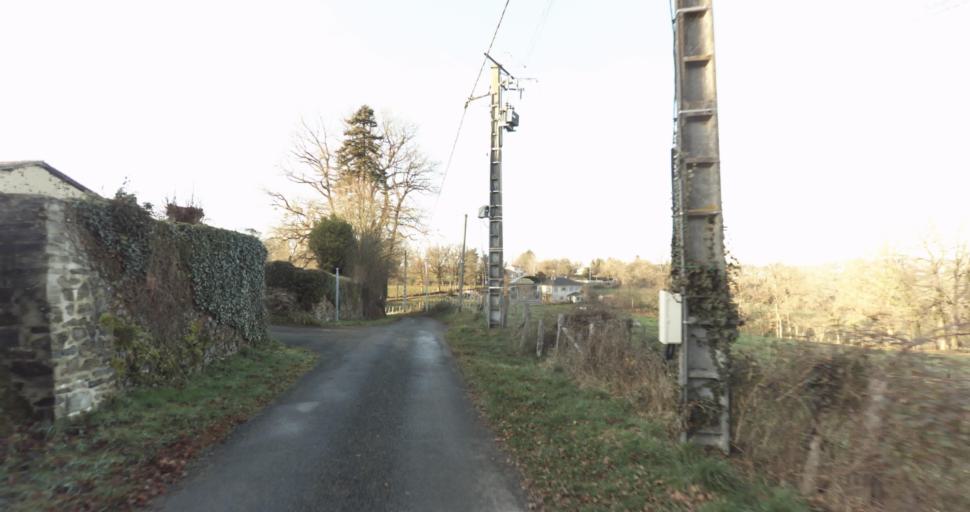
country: FR
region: Limousin
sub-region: Departement de la Haute-Vienne
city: Aixe-sur-Vienne
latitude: 45.7839
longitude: 1.1444
